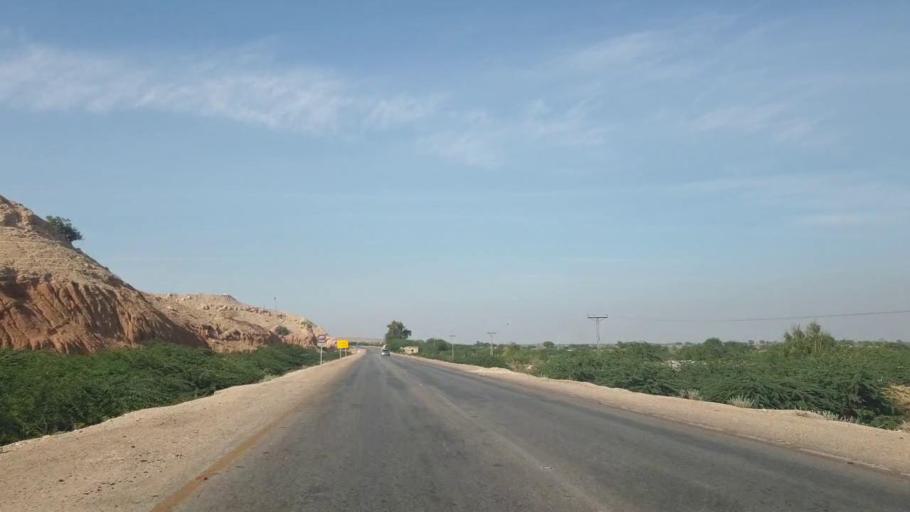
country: PK
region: Sindh
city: Sehwan
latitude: 26.3171
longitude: 67.8892
